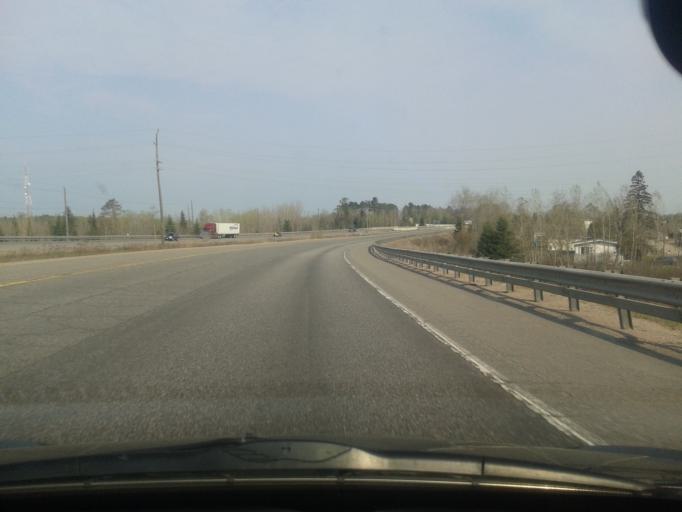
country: CA
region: Ontario
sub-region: Nipissing District
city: North Bay
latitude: 46.2692
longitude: -79.3983
